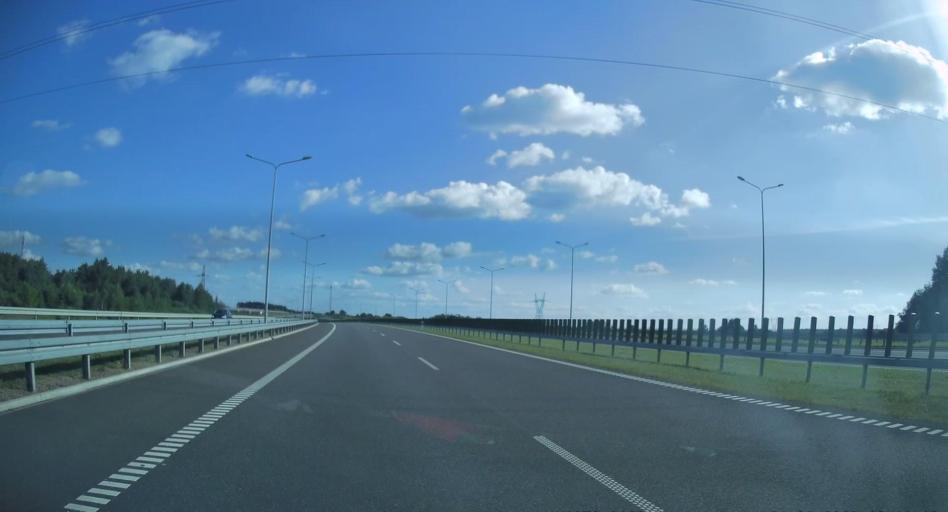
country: PL
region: Masovian Voivodeship
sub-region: Powiat szydlowiecki
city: Oronsko
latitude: 51.3378
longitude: 21.0145
